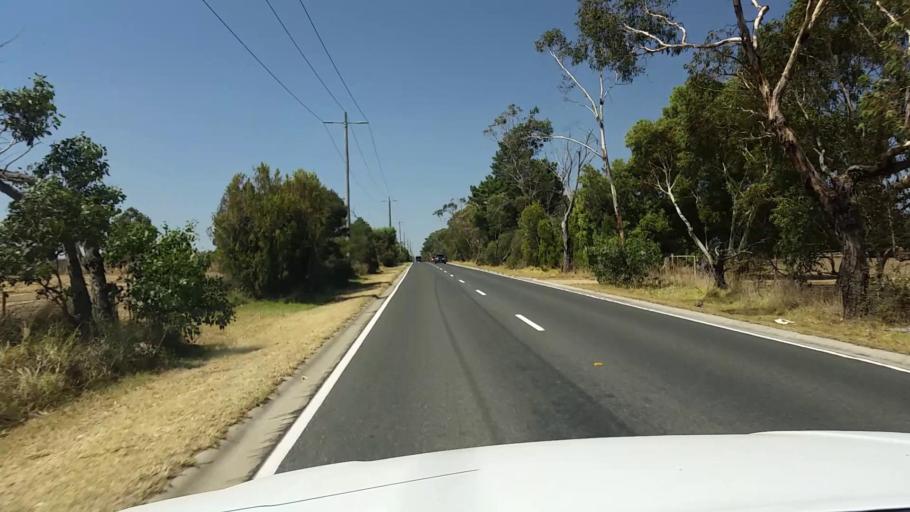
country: AU
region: Victoria
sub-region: Mornington Peninsula
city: Moorooduc
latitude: -38.2327
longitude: 145.1344
